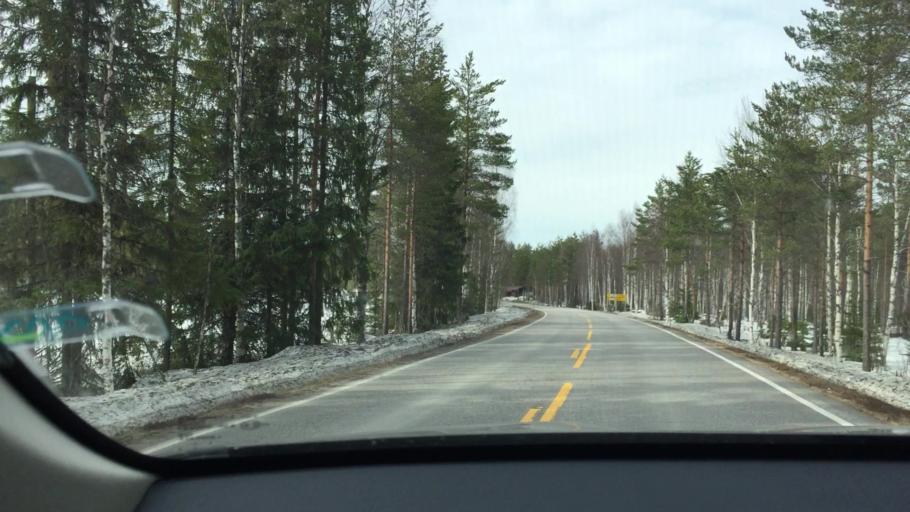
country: NO
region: Hedmark
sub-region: Trysil
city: Innbygda
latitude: 61.0726
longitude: 12.5779
